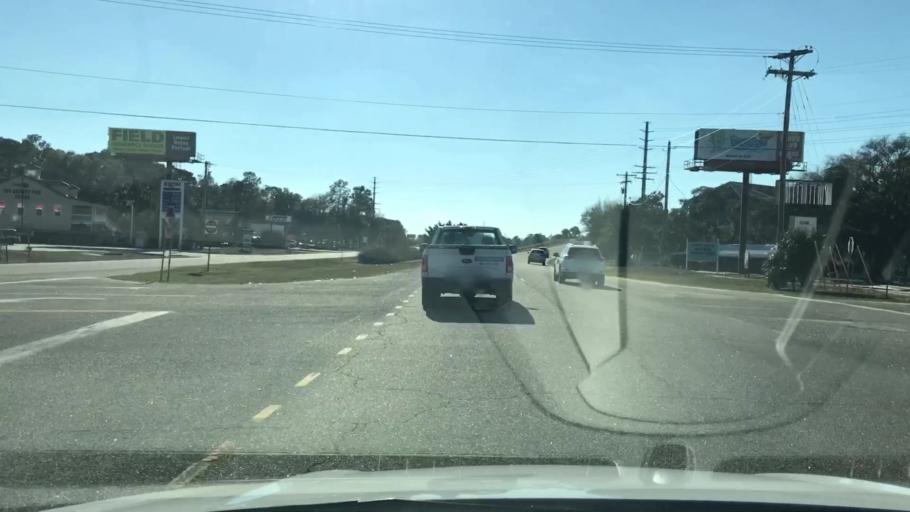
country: US
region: South Carolina
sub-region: Horry County
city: Garden City
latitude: 33.5764
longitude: -79.0259
